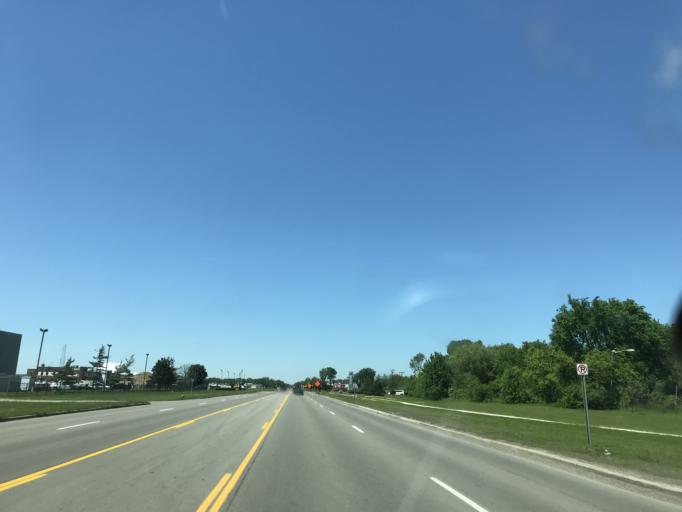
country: US
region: Michigan
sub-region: Wayne County
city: Taylor
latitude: 42.2273
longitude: -83.3274
